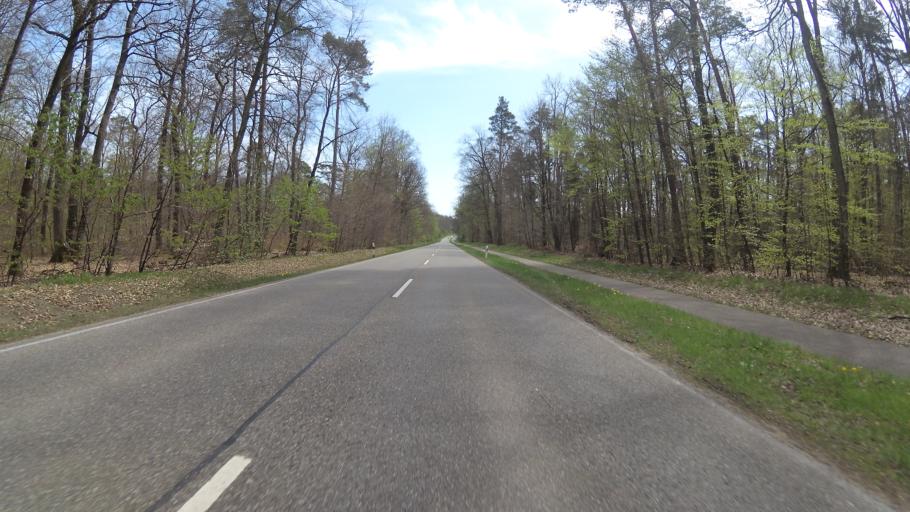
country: DE
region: Rheinland-Pfalz
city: Waldmohr
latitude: 49.3620
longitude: 7.3261
